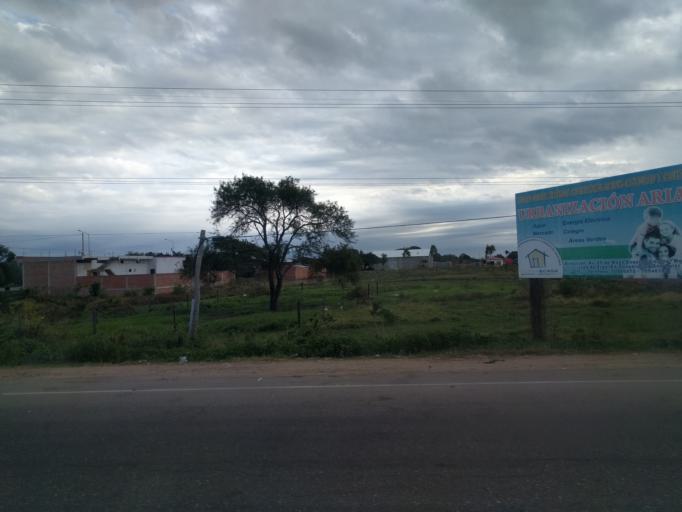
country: BO
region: Santa Cruz
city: Warnes
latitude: -17.5043
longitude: -63.1708
